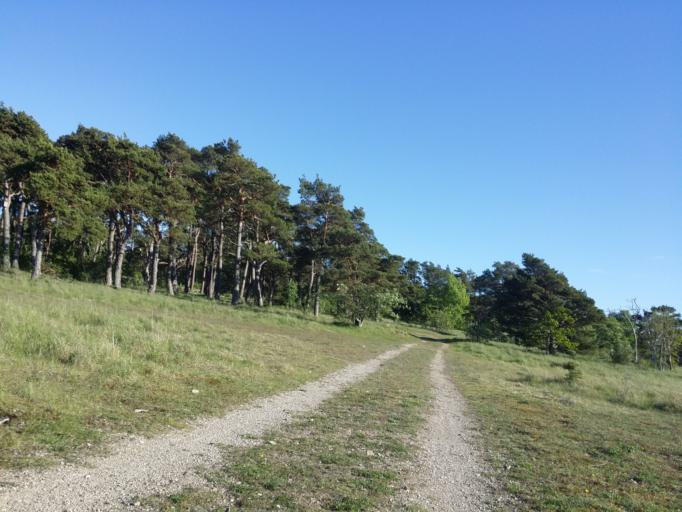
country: SE
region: Gotland
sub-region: Gotland
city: Vibble
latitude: 57.6188
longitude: 18.2654
